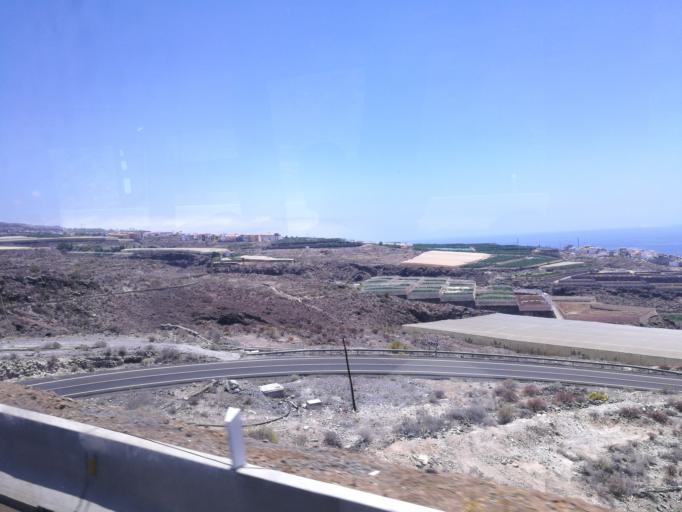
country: ES
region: Canary Islands
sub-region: Provincia de Santa Cruz de Tenerife
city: Guia de Isora
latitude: 28.1905
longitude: -16.7999
